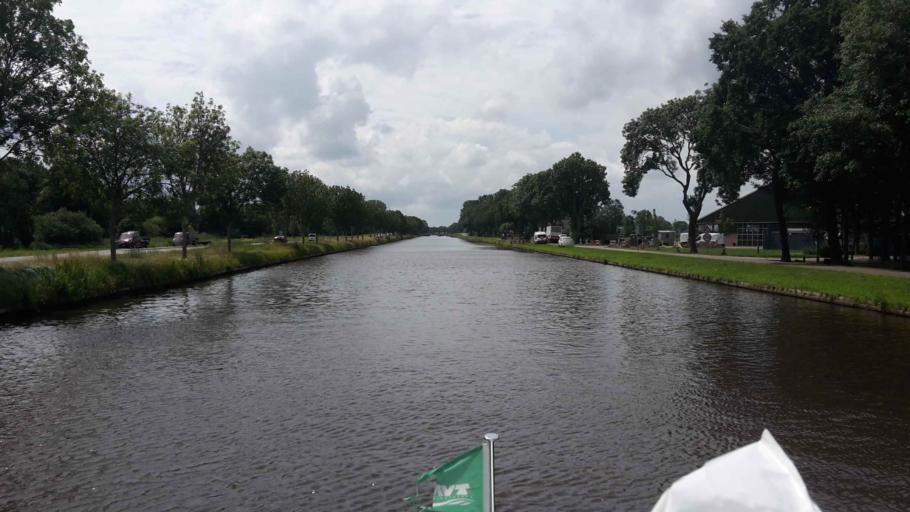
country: NL
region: Overijssel
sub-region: Gemeente Steenwijkerland
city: Giethoorn
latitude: 52.7503
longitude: 6.0780
